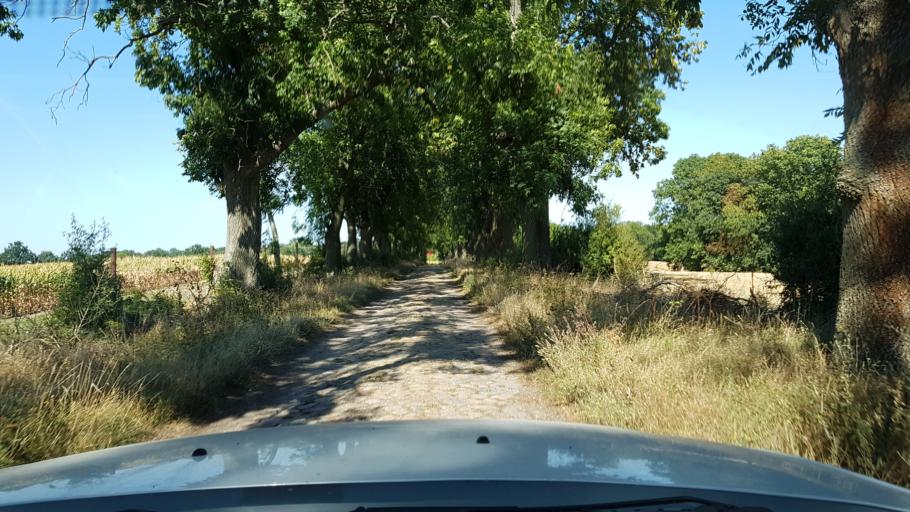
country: PL
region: West Pomeranian Voivodeship
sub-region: Powiat gryfinski
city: Cedynia
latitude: 52.8607
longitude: 14.2254
